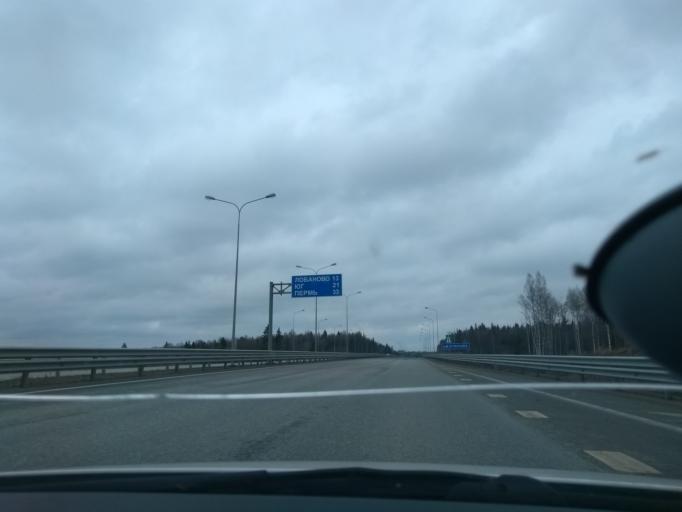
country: RU
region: Perm
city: Zvezdnyy
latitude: 57.7365
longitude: 56.3428
